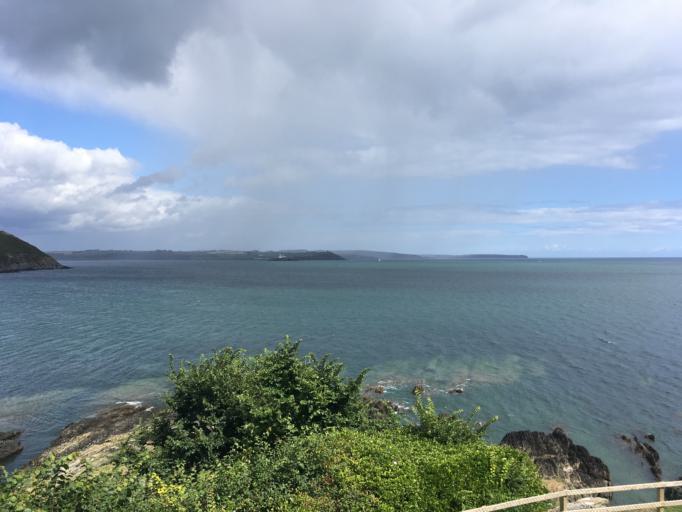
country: IE
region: Munster
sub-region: County Cork
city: Crosshaven
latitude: 51.7809
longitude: -8.2936
